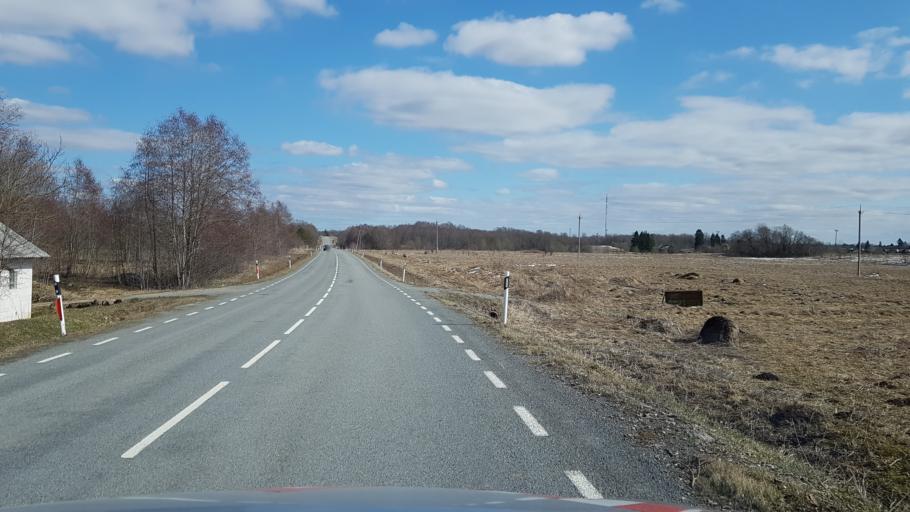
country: EE
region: Laeaene-Virumaa
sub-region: Tapa vald
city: Tapa
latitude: 59.2690
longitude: 25.9315
